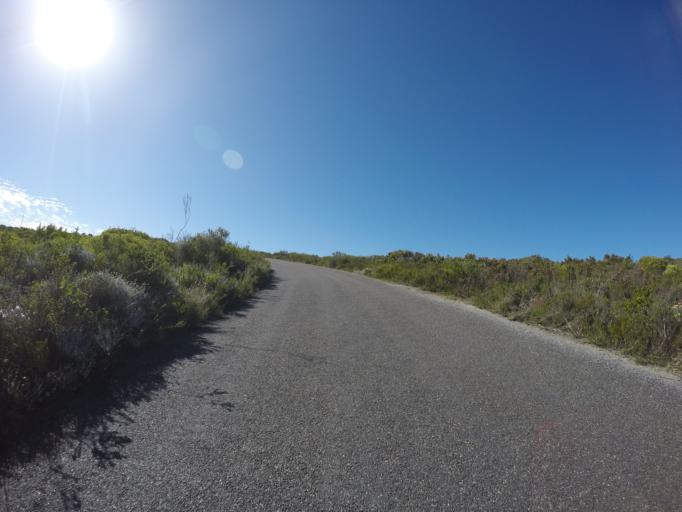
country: ZA
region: Western Cape
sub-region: Overberg District Municipality
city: Bredasdorp
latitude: -34.4248
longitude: 20.4137
